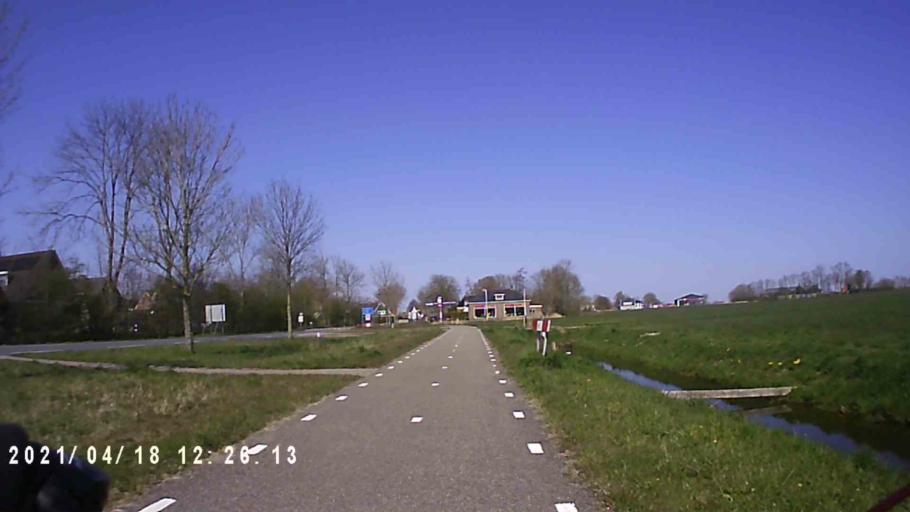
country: NL
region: Friesland
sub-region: Gemeente Dongeradeel
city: Anjum
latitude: 53.3292
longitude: 6.1065
